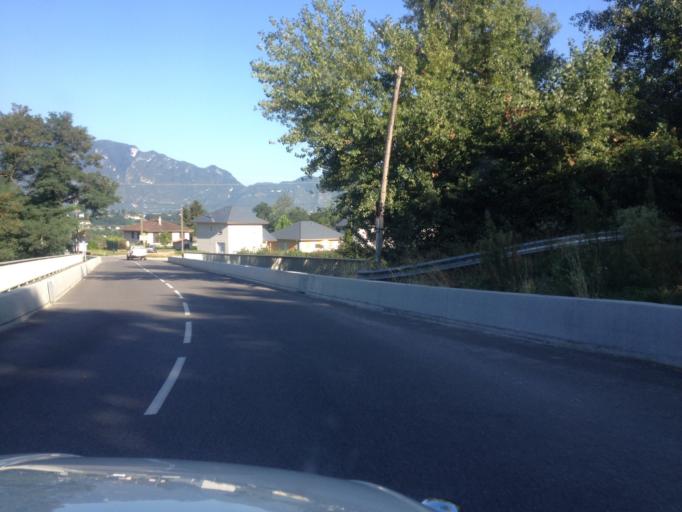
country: FR
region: Rhone-Alpes
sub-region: Departement de la Savoie
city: Drumettaz-Clarafond
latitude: 45.6588
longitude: 5.9270
